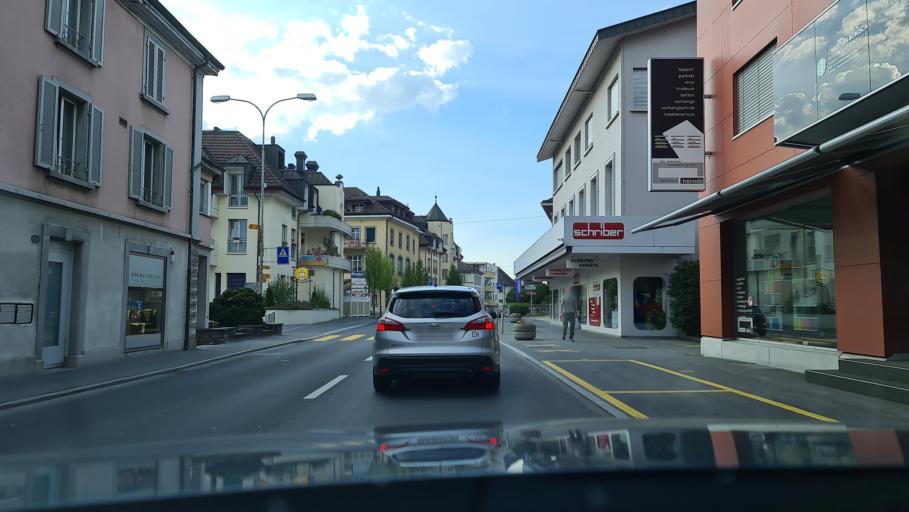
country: CH
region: Lucerne
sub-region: Hochdorf District
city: Hochdorf
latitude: 47.1670
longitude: 8.2893
